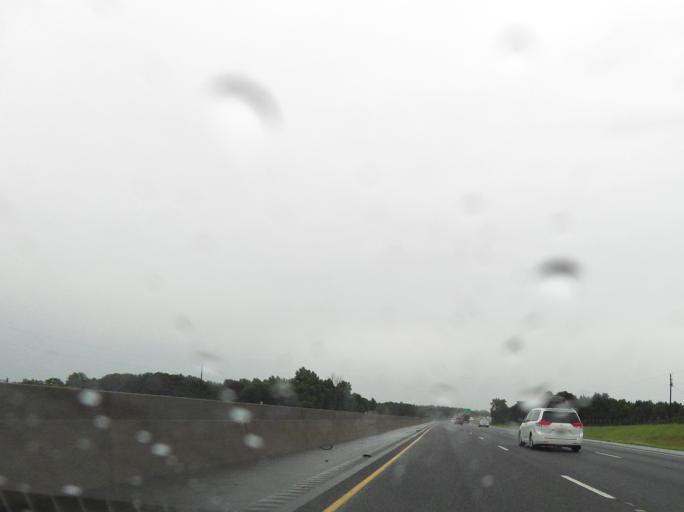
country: US
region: Georgia
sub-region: Tift County
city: Tifton
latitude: 31.5621
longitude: -83.5415
